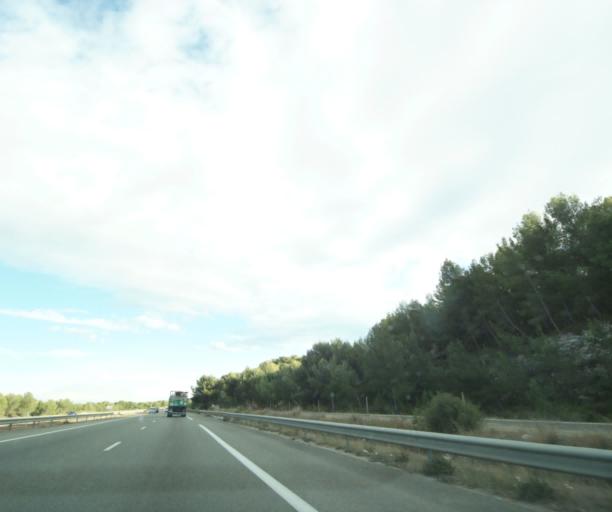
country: FR
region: Provence-Alpes-Cote d'Azur
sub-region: Departement des Bouches-du-Rhone
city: Chateauneuf-les-Martigues
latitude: 43.3887
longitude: 5.1405
